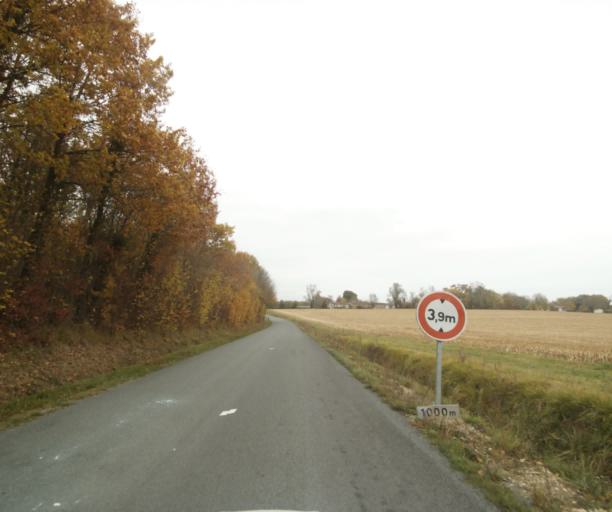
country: FR
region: Poitou-Charentes
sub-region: Departement de la Charente-Maritime
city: Chermignac
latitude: 45.7087
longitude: -0.6907
